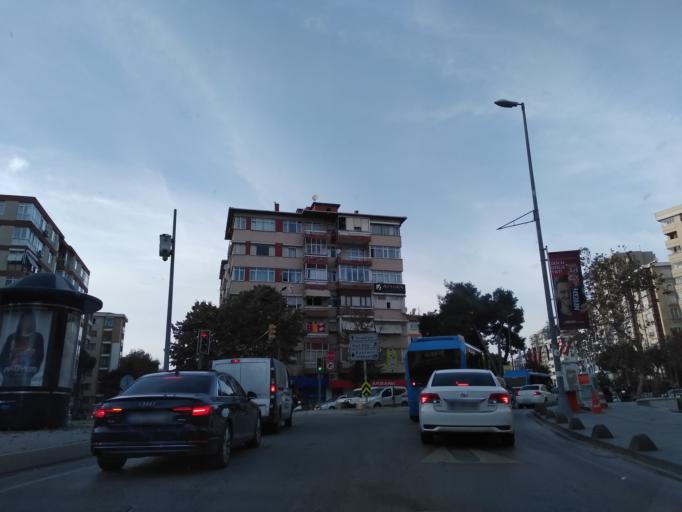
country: TR
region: Istanbul
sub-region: Atasehir
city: Atasehir
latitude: 40.9583
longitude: 29.0956
